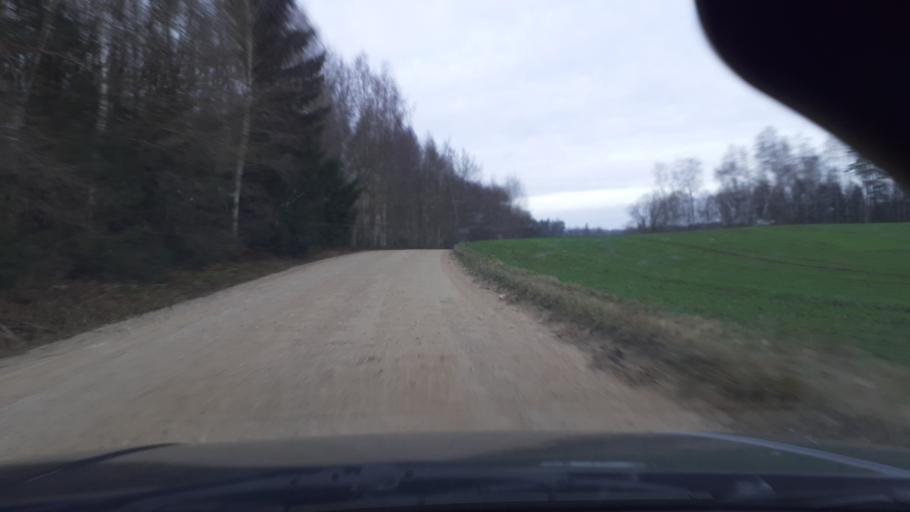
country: LV
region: Alsunga
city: Alsunga
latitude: 56.9579
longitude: 21.6502
